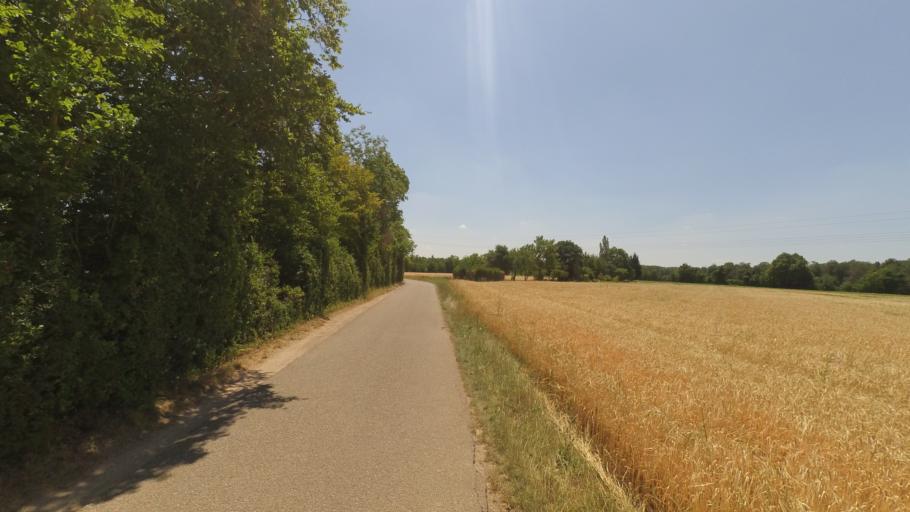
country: DE
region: Baden-Wuerttemberg
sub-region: Karlsruhe Region
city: Schwetzingen
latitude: 49.3809
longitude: 8.5596
